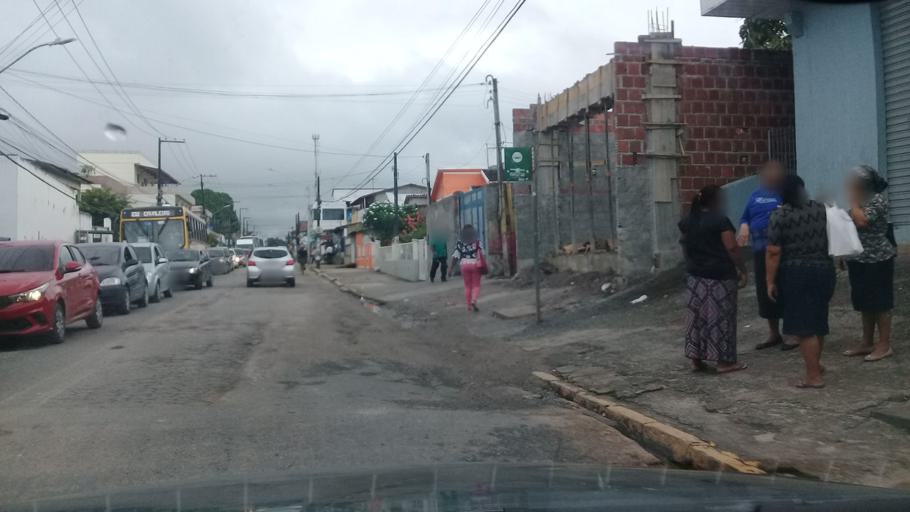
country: BR
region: Pernambuco
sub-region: Jaboatao Dos Guararapes
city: Jaboatao dos Guararapes
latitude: -8.0991
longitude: -34.9702
